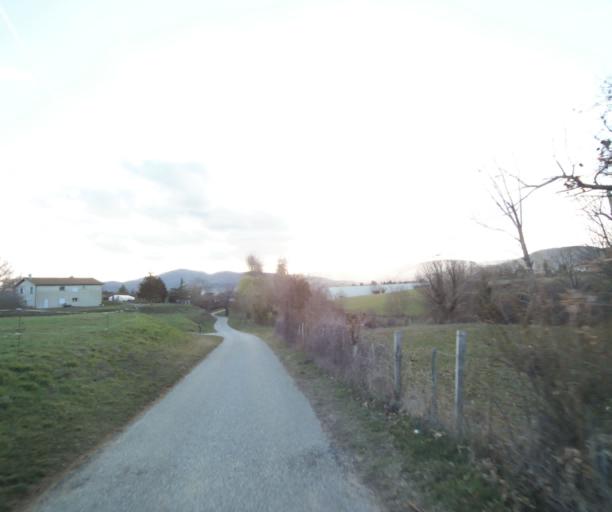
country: FR
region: Rhone-Alpes
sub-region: Departement de l'Ardeche
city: Davezieux
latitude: 45.2440
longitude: 4.6960
